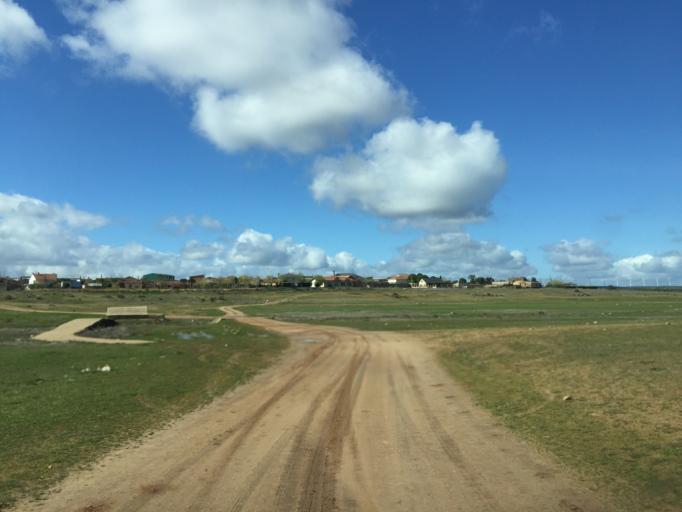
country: ES
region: Castille and Leon
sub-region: Provincia de Zamora
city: Montamarta
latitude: 41.6525
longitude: -5.8068
